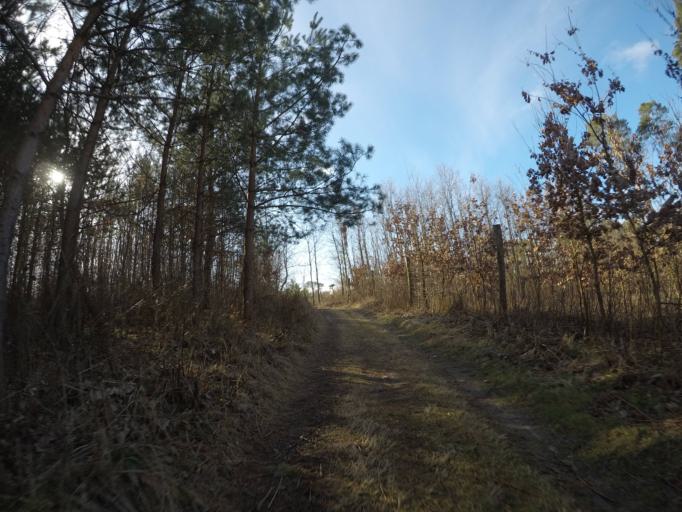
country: PL
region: Kujawsko-Pomorskie
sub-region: Powiat brodnicki
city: Gorzno
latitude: 53.1919
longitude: 19.6570
